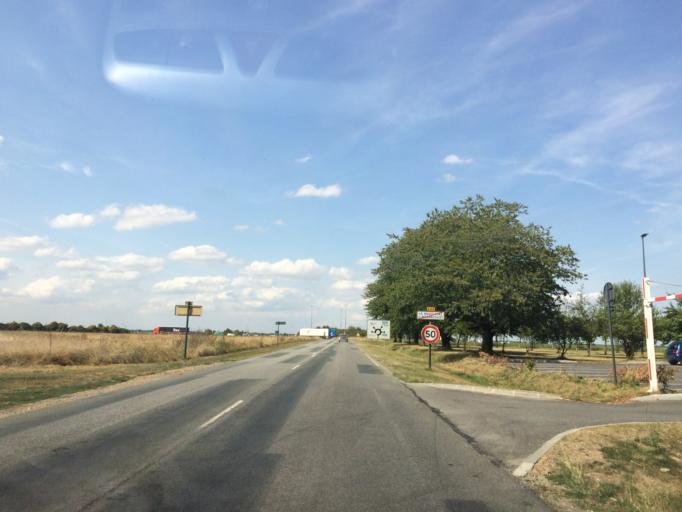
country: FR
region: Haute-Normandie
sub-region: Departement de l'Eure
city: Nonancourt
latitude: 48.7781
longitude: 1.1943
